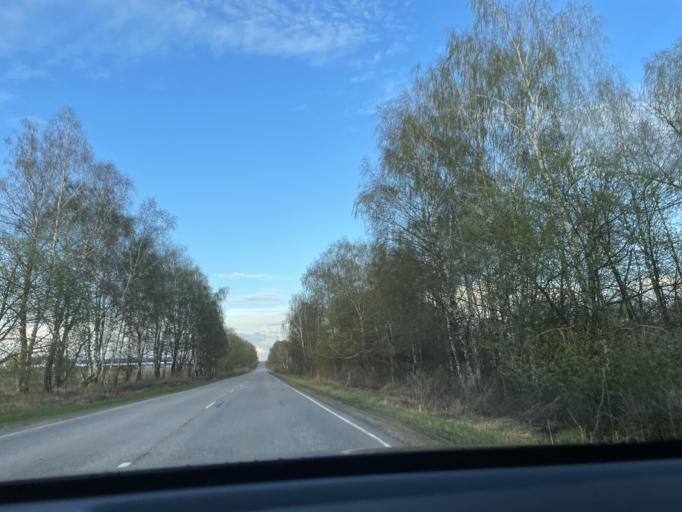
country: RU
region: Tula
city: Novogurovskiy
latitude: 54.5292
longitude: 37.3366
